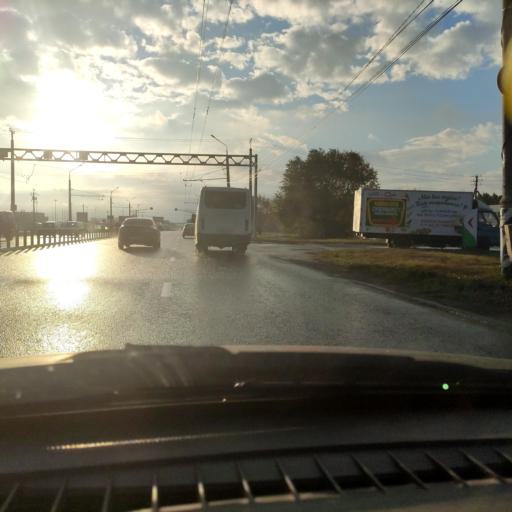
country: RU
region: Samara
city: Tol'yatti
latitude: 53.5445
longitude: 49.3814
